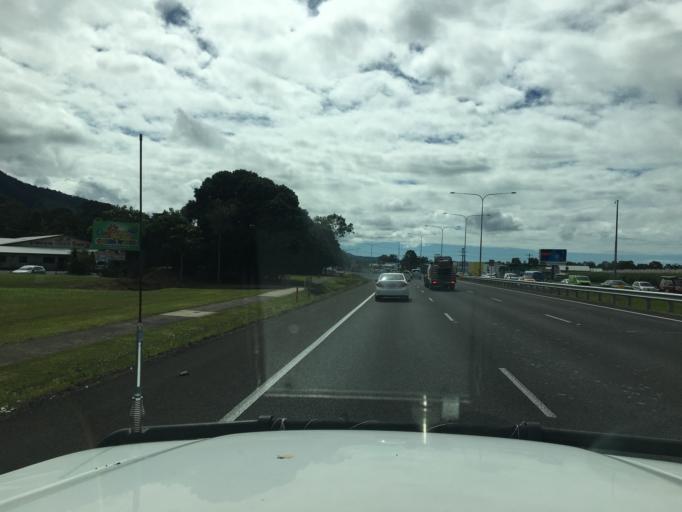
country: AU
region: Queensland
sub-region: Cairns
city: Woree
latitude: -17.0072
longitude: 145.7443
